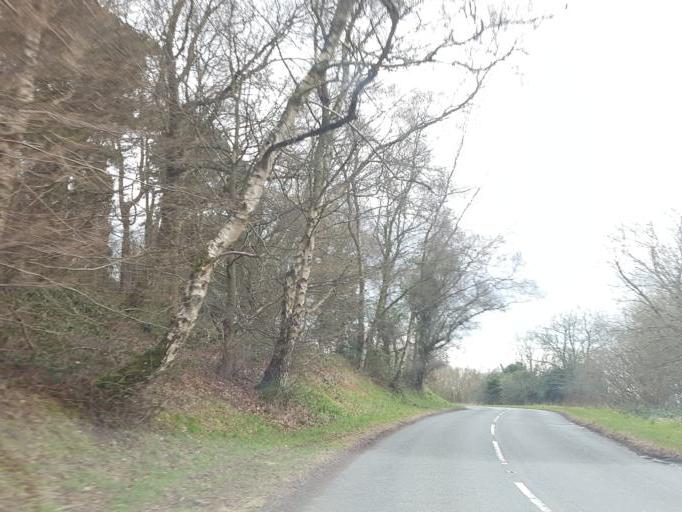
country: GB
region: England
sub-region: Worcestershire
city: Great Malvern
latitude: 52.1008
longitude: -2.3424
